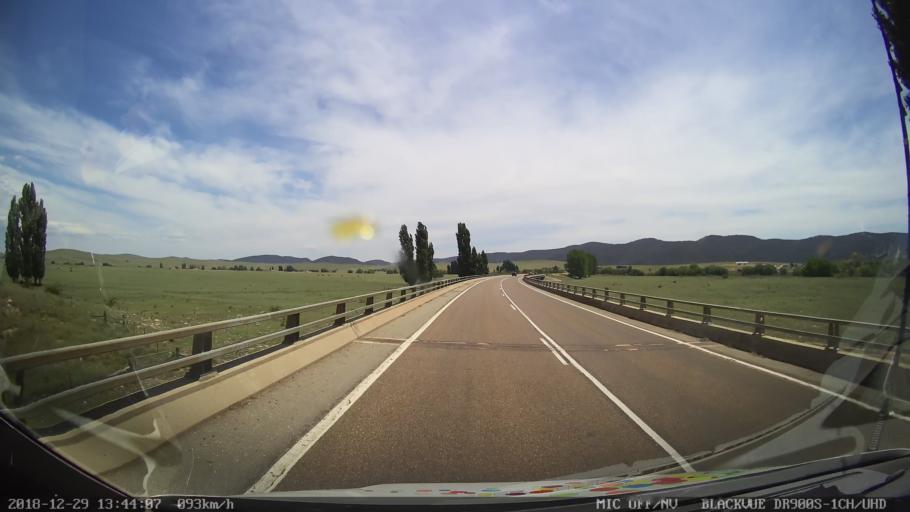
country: AU
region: New South Wales
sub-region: Cooma-Monaro
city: Cooma
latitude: -36.0814
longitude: 149.1568
